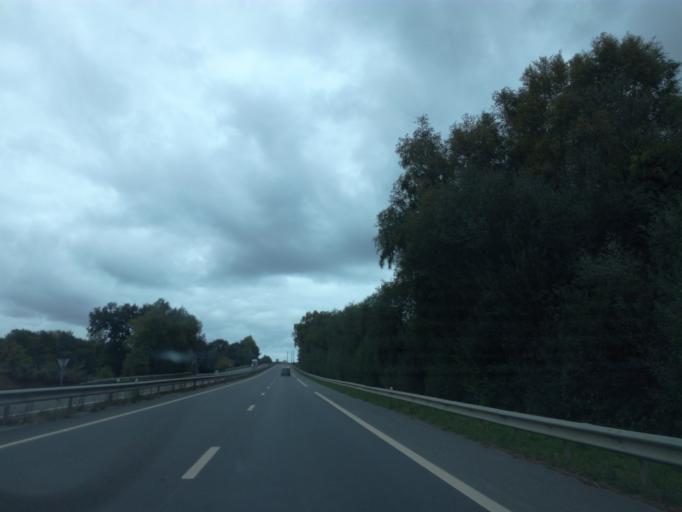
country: FR
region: Brittany
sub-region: Departement des Cotes-d'Armor
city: Saint-Barnabe
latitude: 48.1753
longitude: -2.6568
